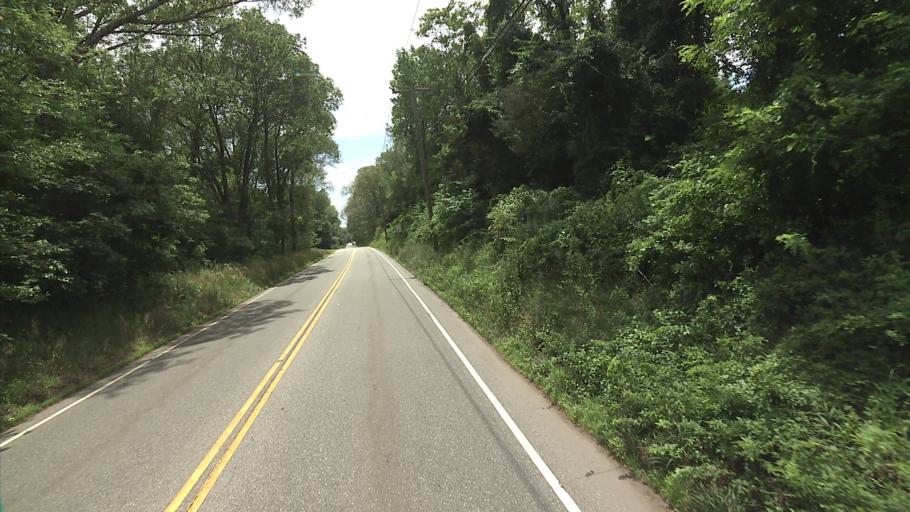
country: US
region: Connecticut
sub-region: New London County
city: Preston City
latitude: 41.5006
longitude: -71.9846
